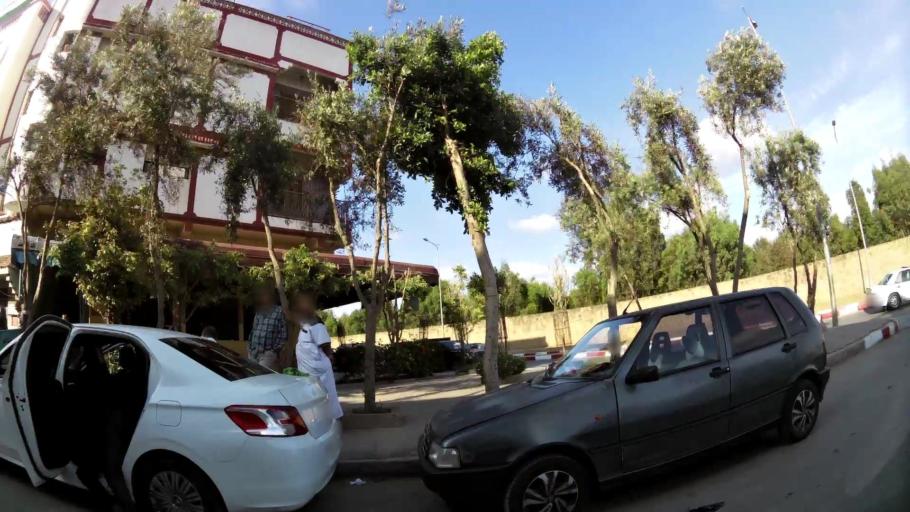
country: MA
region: Rabat-Sale-Zemmour-Zaer
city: Sale
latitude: 34.0509
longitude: -6.7740
